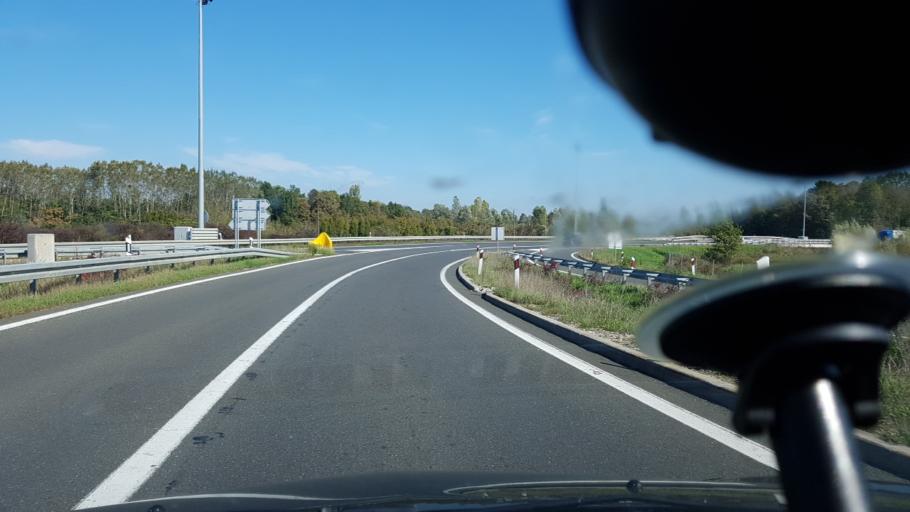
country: HR
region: Zagrebacka
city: Brckovljani
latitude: 45.7657
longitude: 16.2272
